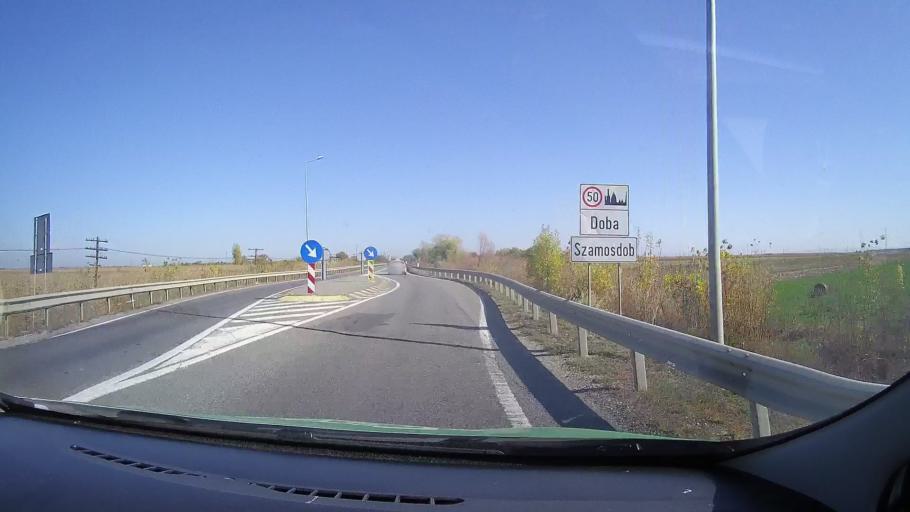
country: RO
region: Satu Mare
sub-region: Comuna Doba
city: Doba
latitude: 47.7355
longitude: 22.6970
